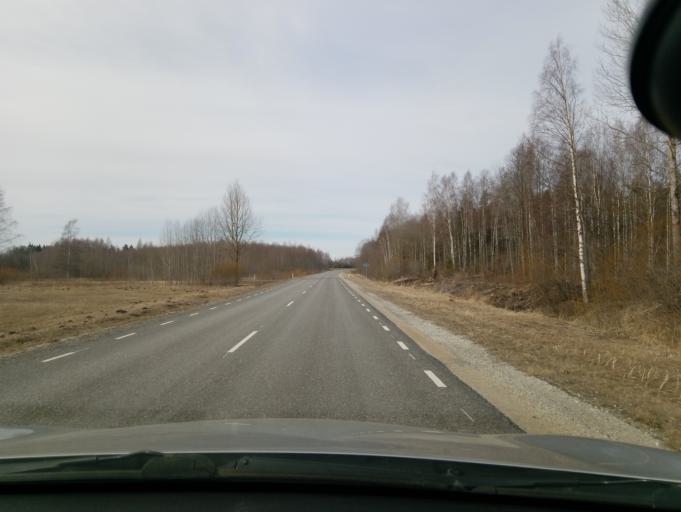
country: EE
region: Jaervamaa
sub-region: Tueri vald
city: Tueri
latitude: 58.8272
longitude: 25.3646
